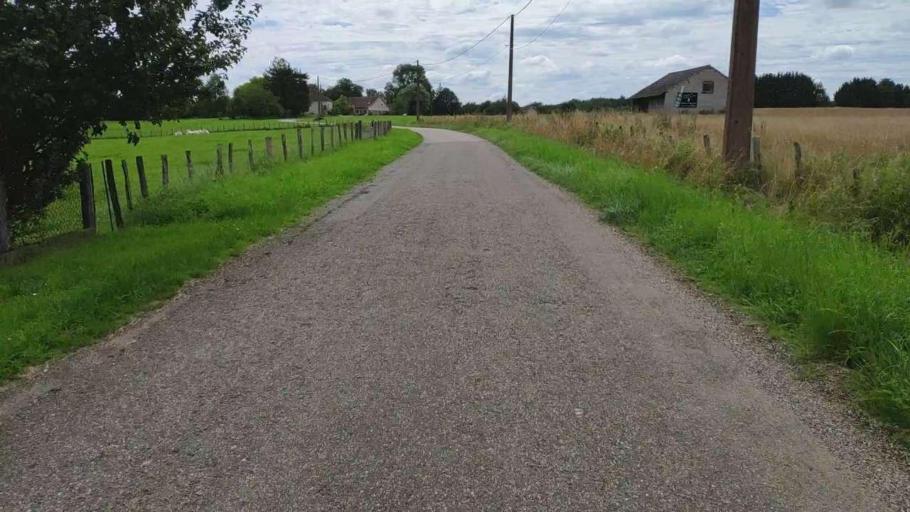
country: FR
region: Franche-Comte
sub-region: Departement du Jura
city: Chaussin
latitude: 46.8810
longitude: 5.4392
